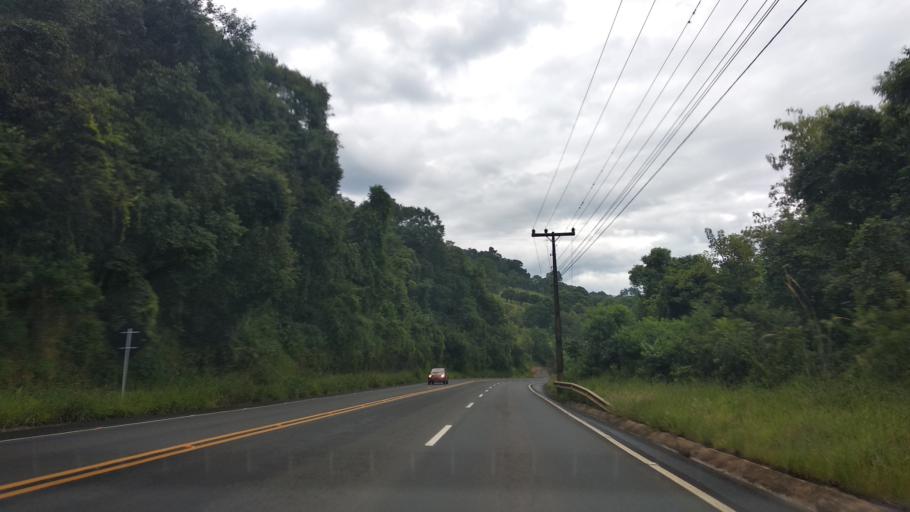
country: BR
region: Santa Catarina
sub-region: Videira
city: Videira
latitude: -27.0634
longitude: -51.2269
